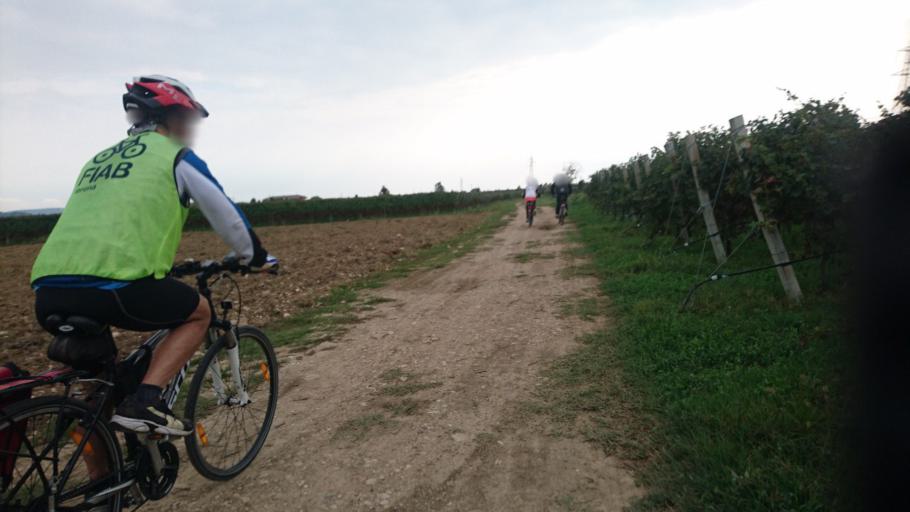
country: IT
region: Veneto
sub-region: Provincia di Verona
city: Caldierino-Rota
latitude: 45.4009
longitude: 11.1368
